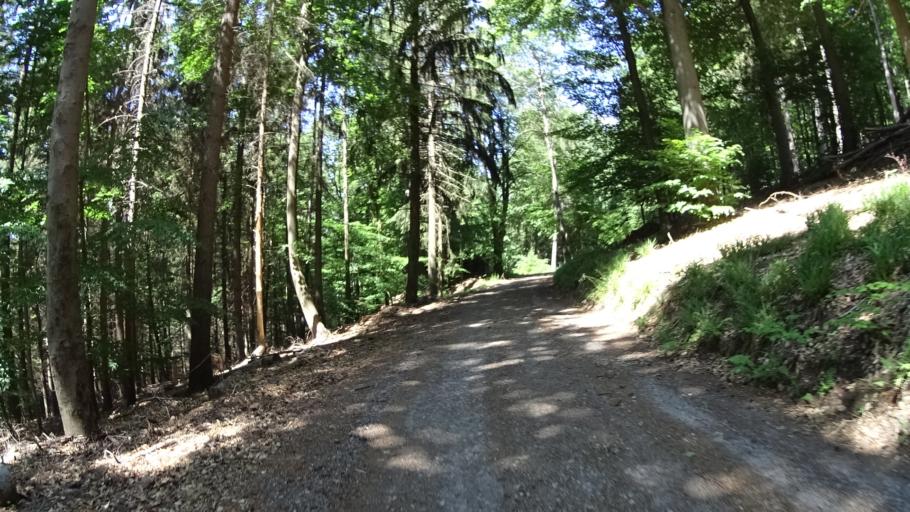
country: DE
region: Baden-Wuerttemberg
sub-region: Karlsruhe Region
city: Neckargemund
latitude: 49.4176
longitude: 8.7821
